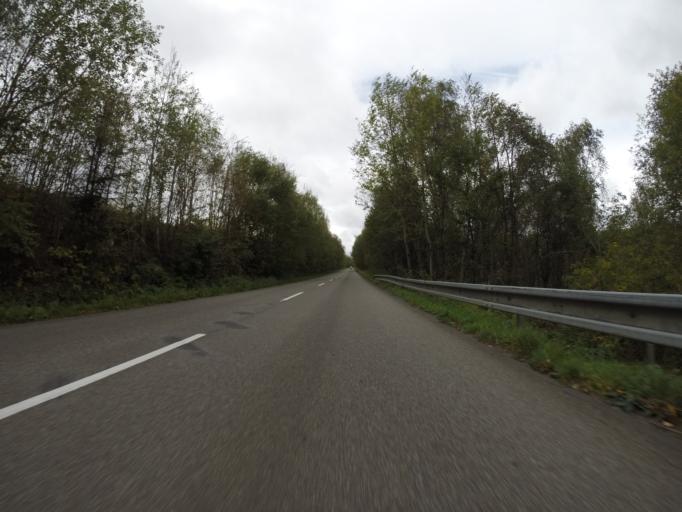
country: SK
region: Banskobystricky
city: Poltar
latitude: 48.5878
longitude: 19.7498
